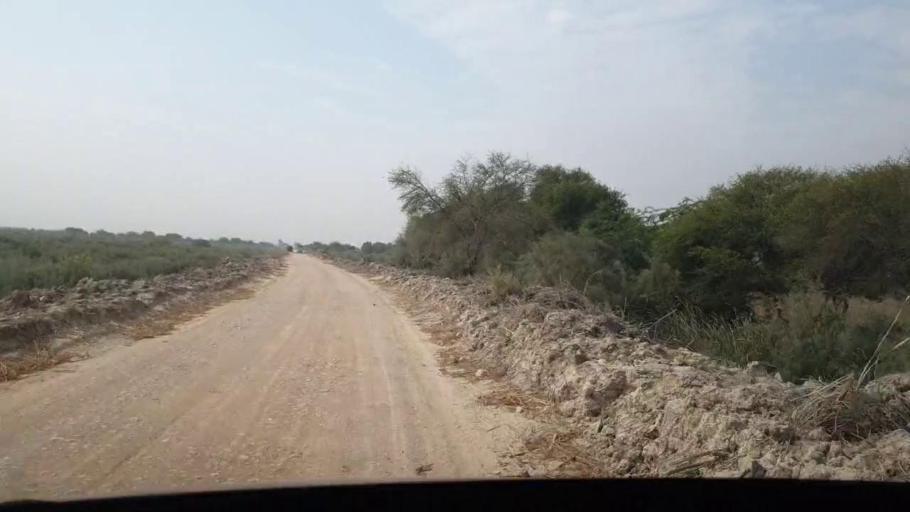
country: PK
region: Sindh
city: Chuhar Jamali
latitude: 24.3692
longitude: 67.9431
